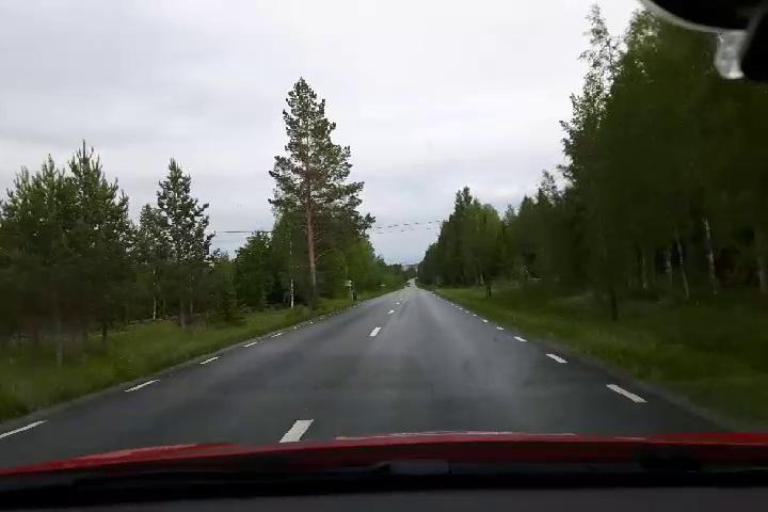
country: SE
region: Jaemtland
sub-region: Bergs Kommun
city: Hoverberg
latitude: 62.9878
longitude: 14.4347
